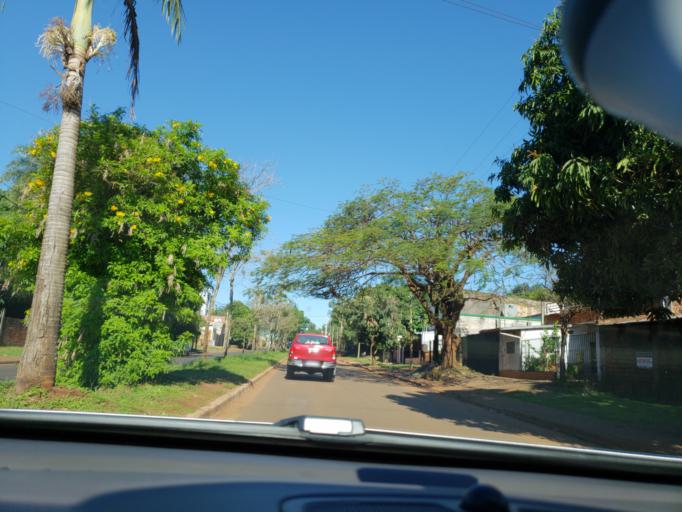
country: AR
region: Misiones
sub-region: Departamento de Capital
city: Posadas
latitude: -27.3852
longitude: -55.9227
